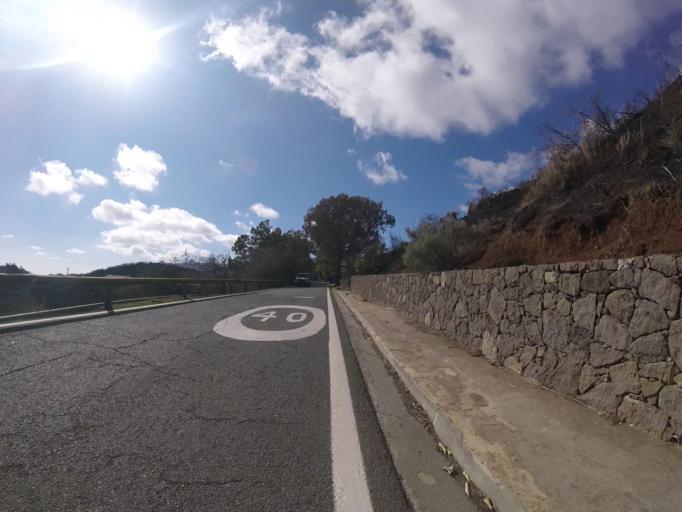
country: ES
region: Canary Islands
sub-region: Provincia de Las Palmas
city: Valleseco
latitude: 28.0144
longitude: -15.5835
